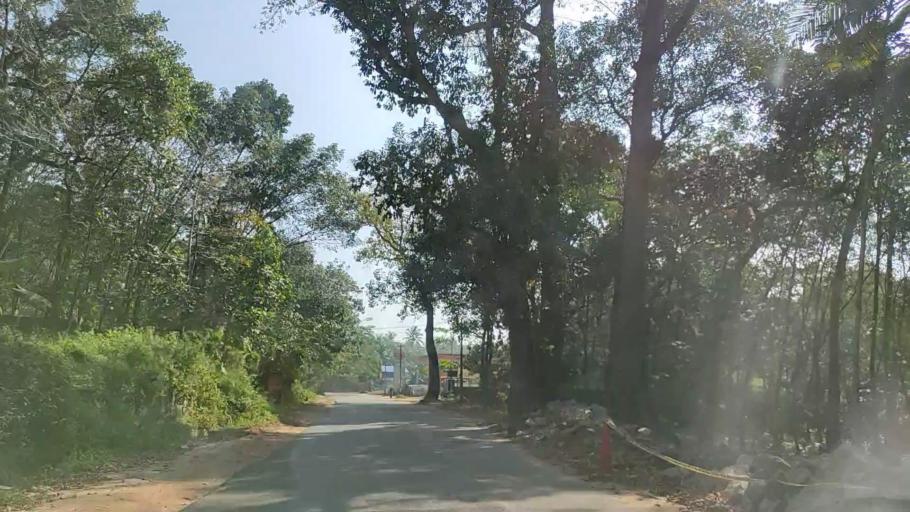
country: IN
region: Kerala
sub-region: Kollam
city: Punalur
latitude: 8.9100
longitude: 76.8794
